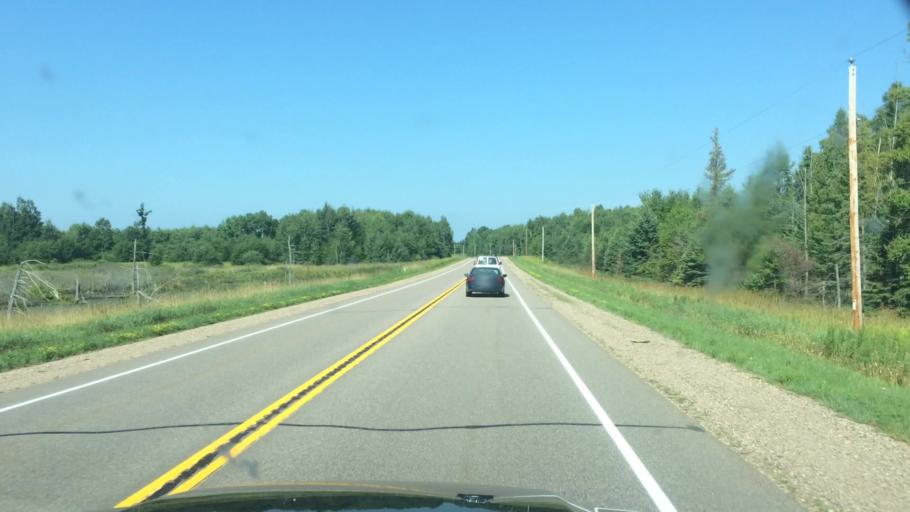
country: US
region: Wisconsin
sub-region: Langlade County
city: Antigo
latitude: 45.1481
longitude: -89.4134
